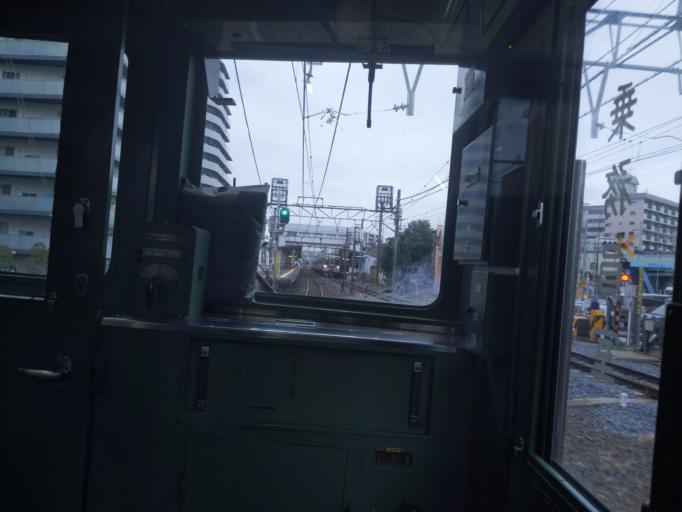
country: JP
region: Saitama
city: Soka
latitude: 35.7444
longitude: 139.8098
